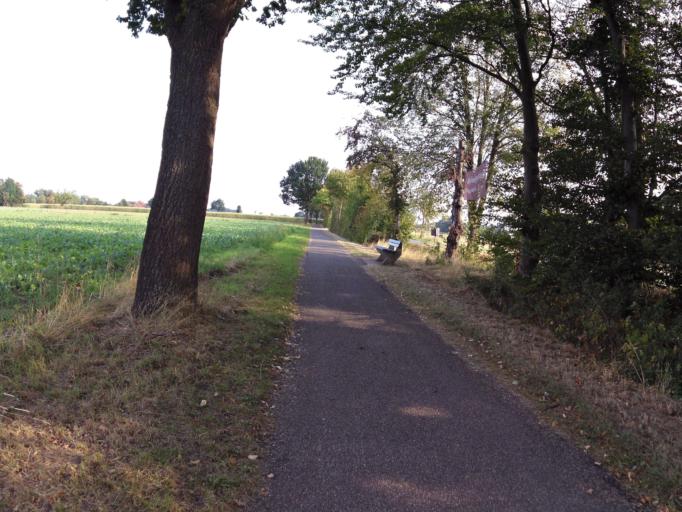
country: DE
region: North Rhine-Westphalia
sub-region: Regierungsbezirk Detmold
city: Petershagen
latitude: 52.3886
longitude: 8.9632
